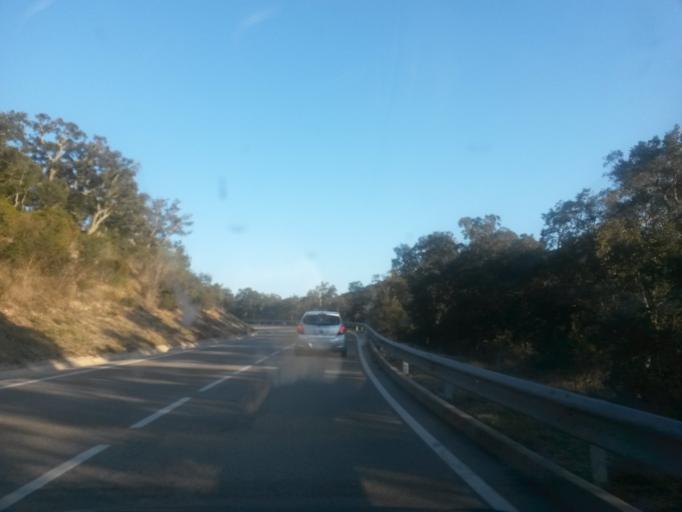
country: ES
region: Catalonia
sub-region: Provincia de Girona
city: Darnius
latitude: 42.3735
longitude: 2.8043
